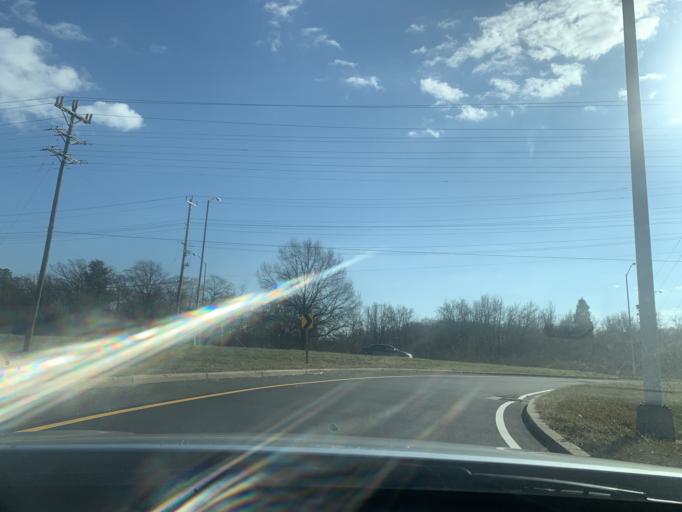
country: US
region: Maryland
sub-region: Prince George's County
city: Oxon Hill
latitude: 38.8097
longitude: -76.9703
